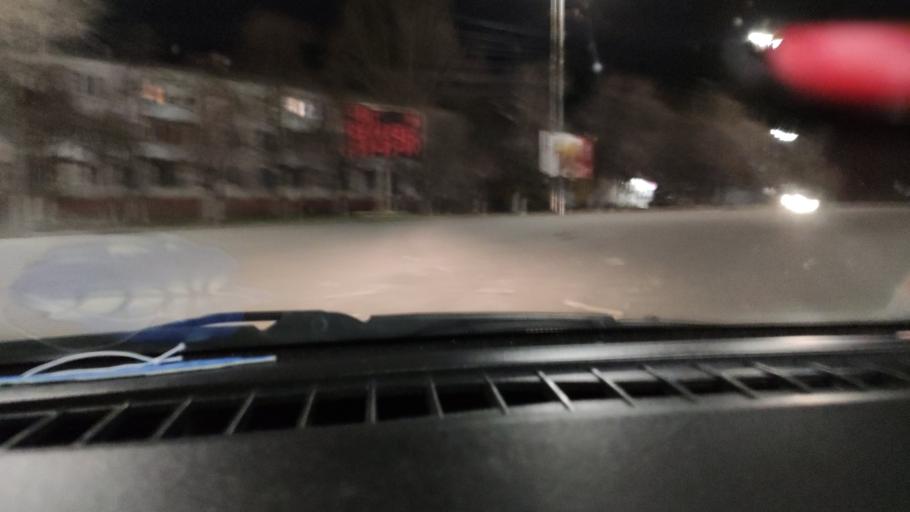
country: RU
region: Saratov
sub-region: Saratovskiy Rayon
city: Saratov
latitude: 51.5585
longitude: 46.0303
